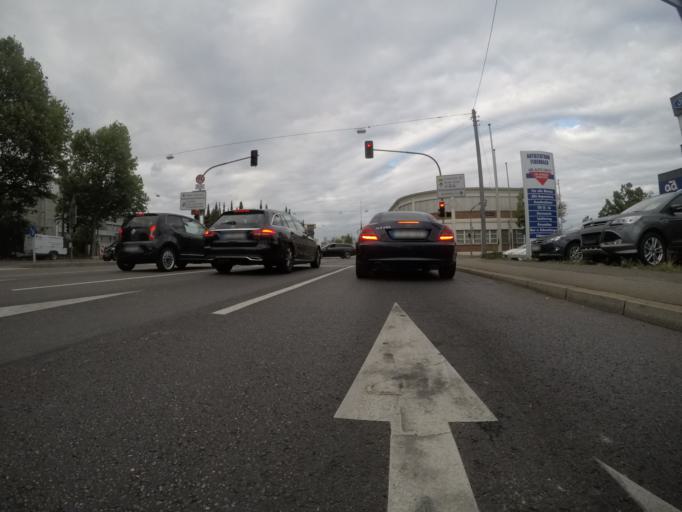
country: DE
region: Baden-Wuerttemberg
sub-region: Regierungsbezirk Stuttgart
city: Stuttgart Feuerbach
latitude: 48.8142
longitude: 9.1601
